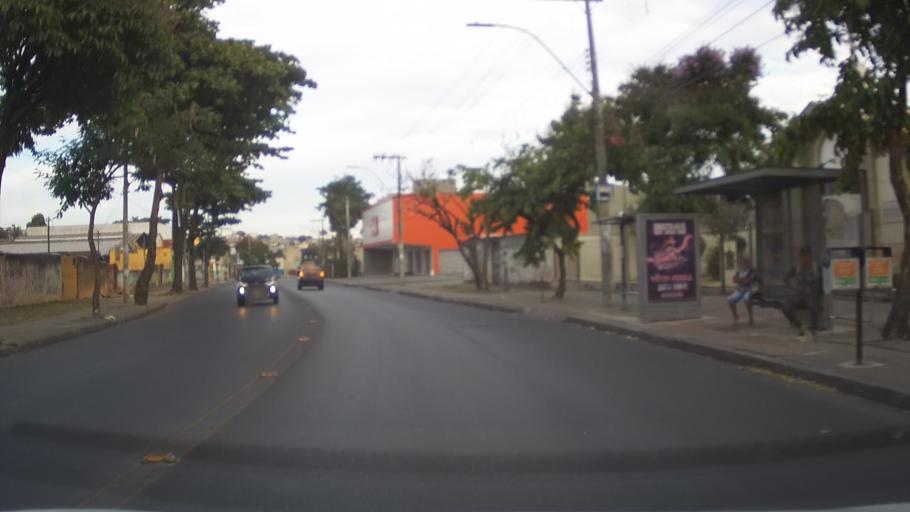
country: BR
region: Minas Gerais
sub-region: Contagem
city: Contagem
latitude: -19.9025
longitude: -44.0063
